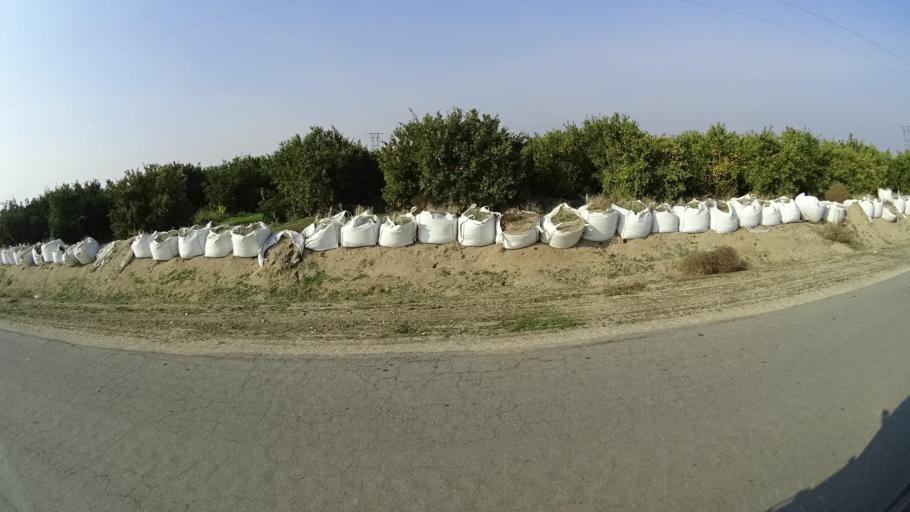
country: US
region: California
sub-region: Kern County
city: Lebec
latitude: 35.0125
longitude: -118.8466
